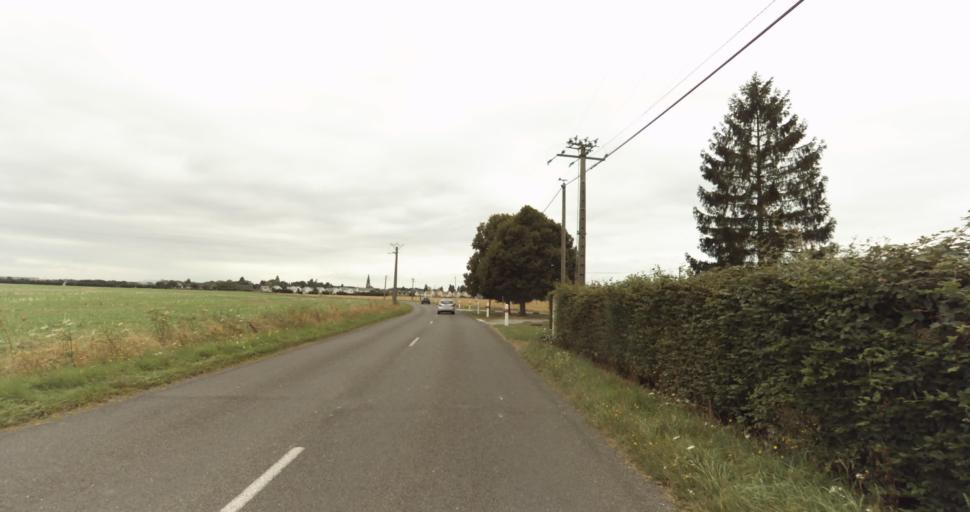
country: FR
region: Haute-Normandie
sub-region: Departement de l'Eure
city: Gravigny
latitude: 49.0437
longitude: 1.2124
